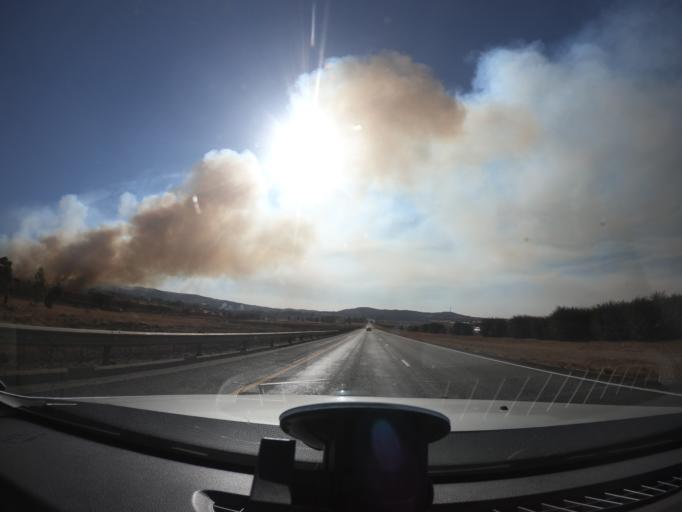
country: ZA
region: Gauteng
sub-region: Sedibeng District Municipality
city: Heidelberg
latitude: -26.5137
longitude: 28.3877
